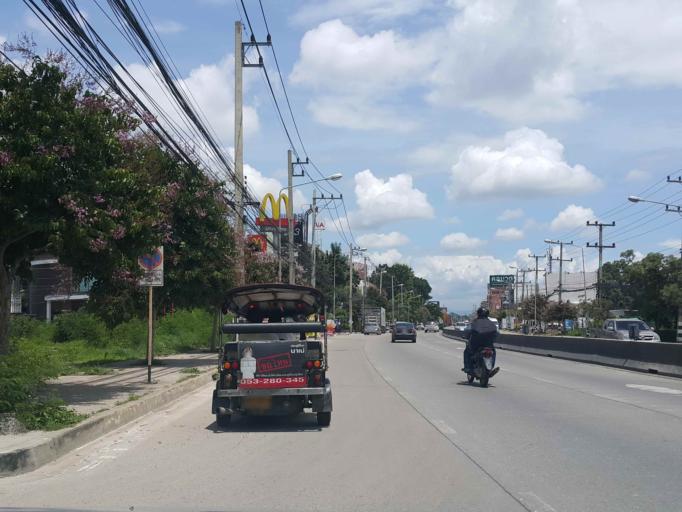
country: TH
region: Chiang Mai
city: Chiang Mai
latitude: 18.7656
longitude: 98.9906
